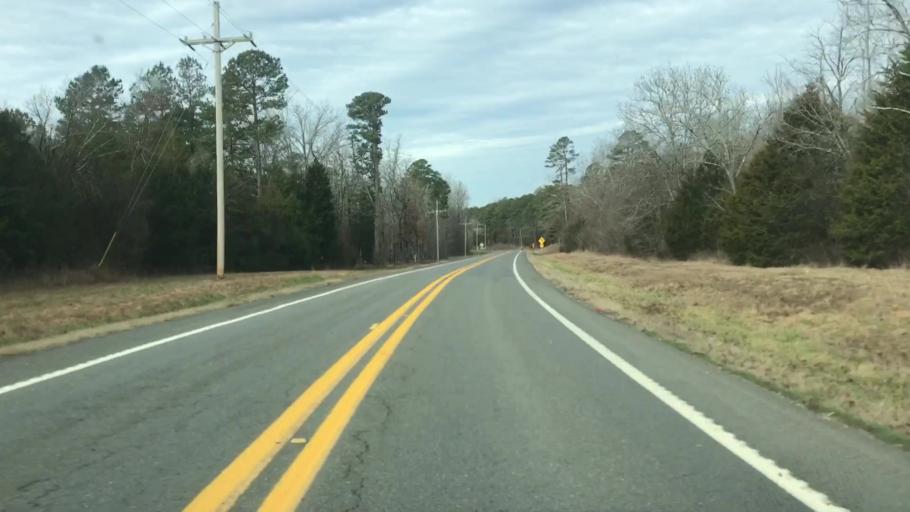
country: US
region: Arkansas
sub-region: Montgomery County
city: Mount Ida
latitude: 34.6085
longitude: -93.6838
